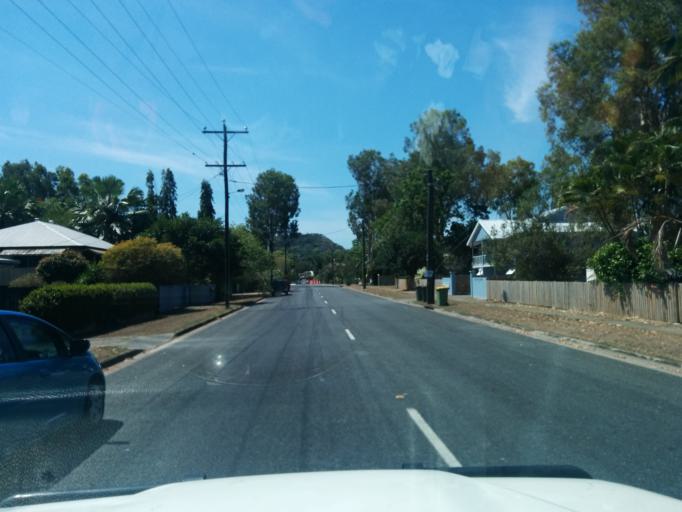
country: AU
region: Queensland
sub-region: Cairns
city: Cairns
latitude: -16.9083
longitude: 145.7554
